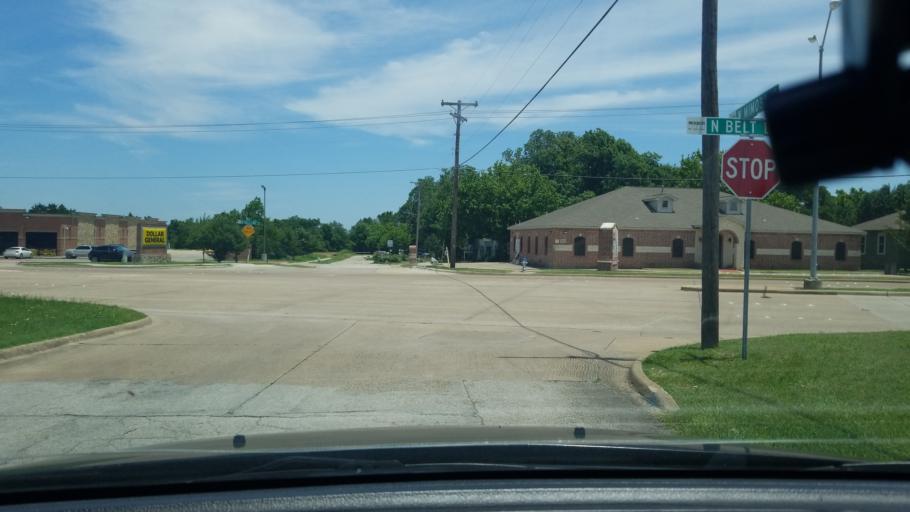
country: US
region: Texas
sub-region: Dallas County
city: Mesquite
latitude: 32.7808
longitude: -96.5967
